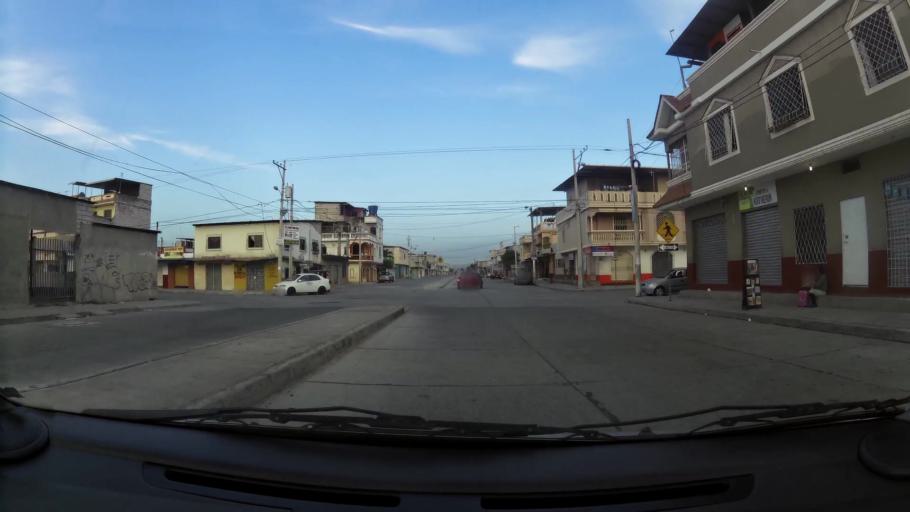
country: EC
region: Guayas
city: Eloy Alfaro
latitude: -2.0882
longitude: -79.9039
